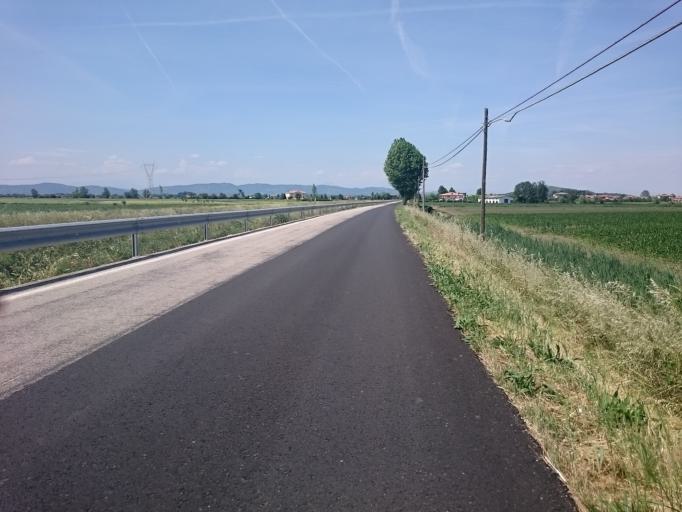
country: IT
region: Veneto
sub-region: Provincia di Padova
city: Lozzo Atestino
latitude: 45.3049
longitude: 11.6033
